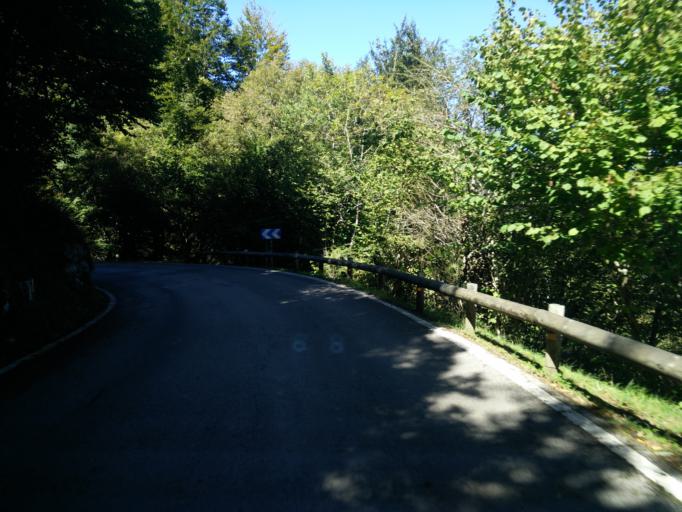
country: ES
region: Cantabria
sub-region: Provincia de Cantabria
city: Ruente
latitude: 43.1152
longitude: -4.2895
